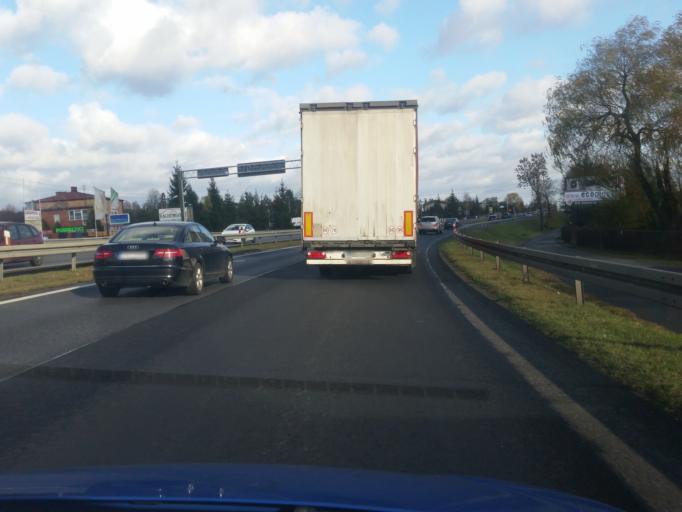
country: PL
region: Silesian Voivodeship
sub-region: Powiat czestochowski
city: Huta Stara B
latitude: 50.7518
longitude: 19.1524
